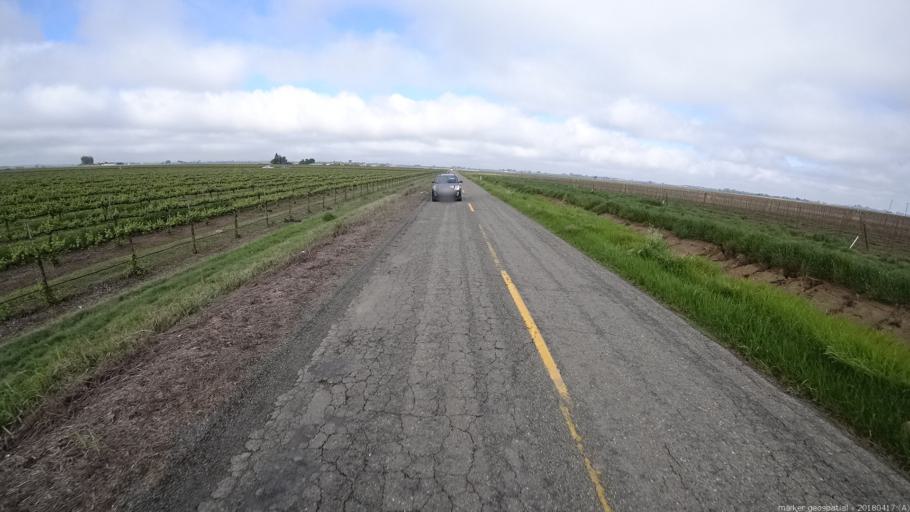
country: US
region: California
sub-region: Sacramento County
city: Walnut Grove
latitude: 38.2127
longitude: -121.5613
